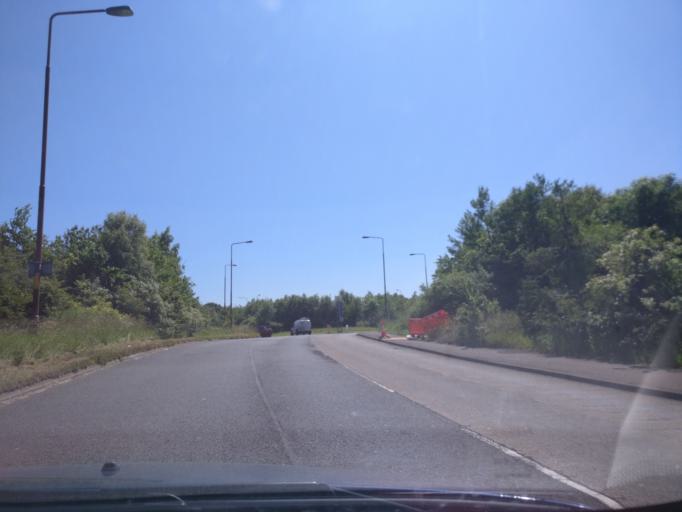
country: GB
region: Scotland
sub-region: East Lothian
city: Tranent
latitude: 55.9544
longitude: -2.9510
